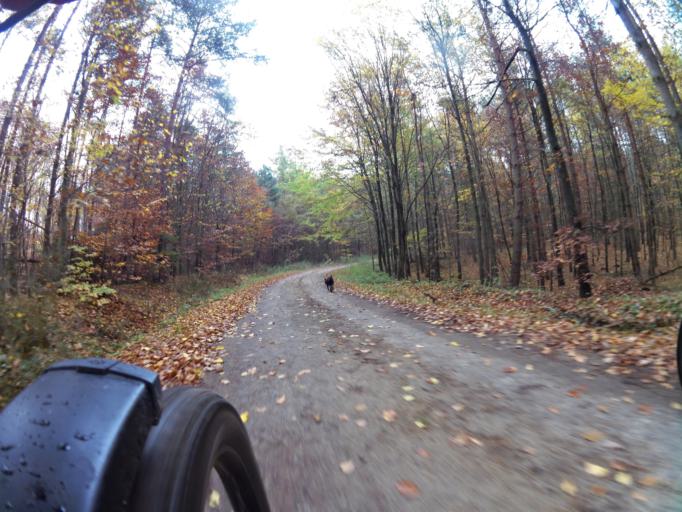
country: PL
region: Pomeranian Voivodeship
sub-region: Powiat pucki
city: Krokowa
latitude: 54.7470
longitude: 18.0946
